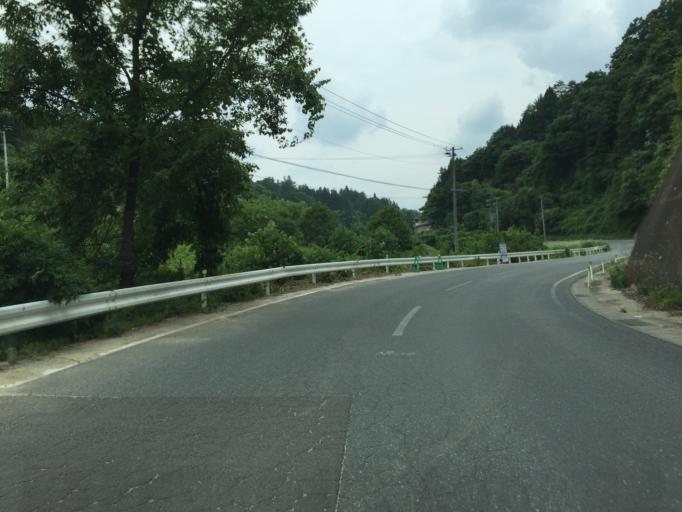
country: JP
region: Fukushima
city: Yanagawamachi-saiwaicho
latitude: 37.7553
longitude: 140.6440
